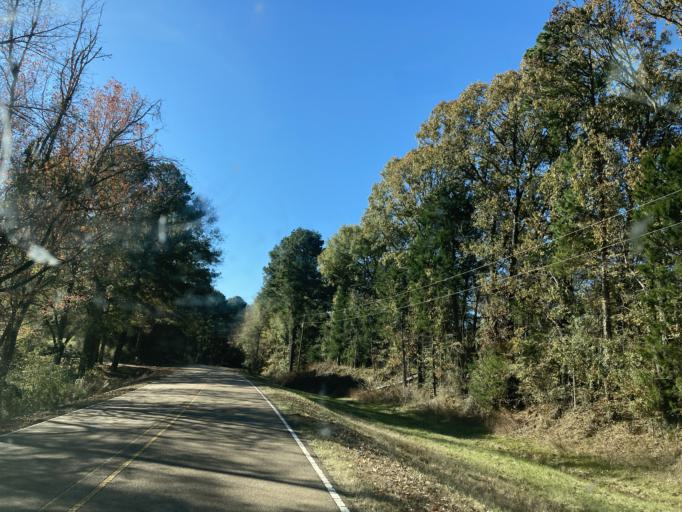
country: US
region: Mississippi
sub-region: Hinds County
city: Lynchburg
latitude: 32.6253
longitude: -90.5218
